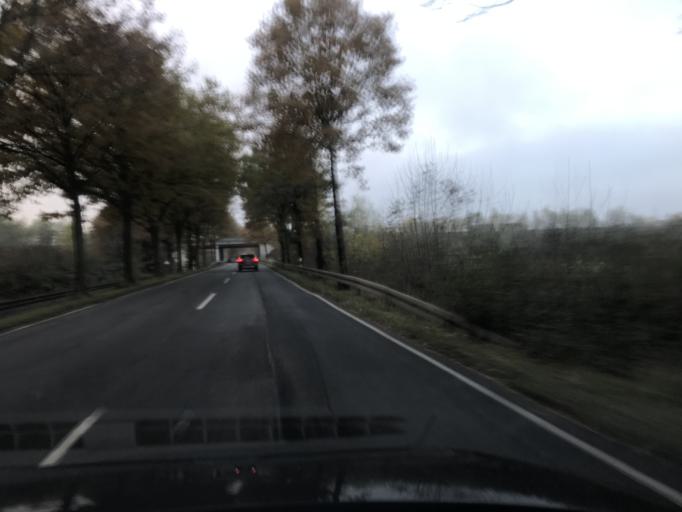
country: DE
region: North Rhine-Westphalia
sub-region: Regierungsbezirk Arnsberg
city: Welver
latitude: 51.6883
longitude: 7.9649
